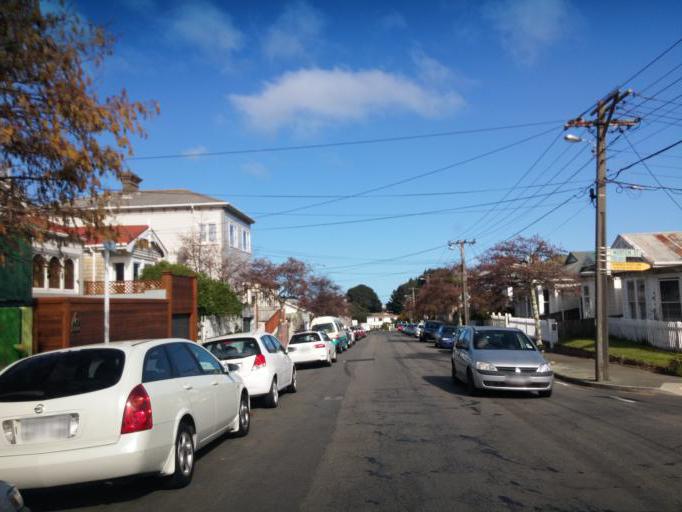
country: NZ
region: Wellington
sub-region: Wellington City
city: Brooklyn
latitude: -41.3212
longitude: 174.7726
